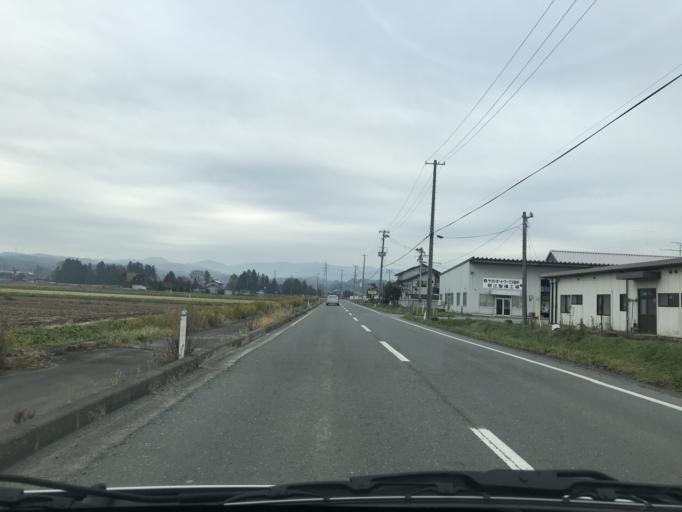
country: JP
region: Iwate
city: Mizusawa
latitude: 39.1596
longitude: 141.1892
